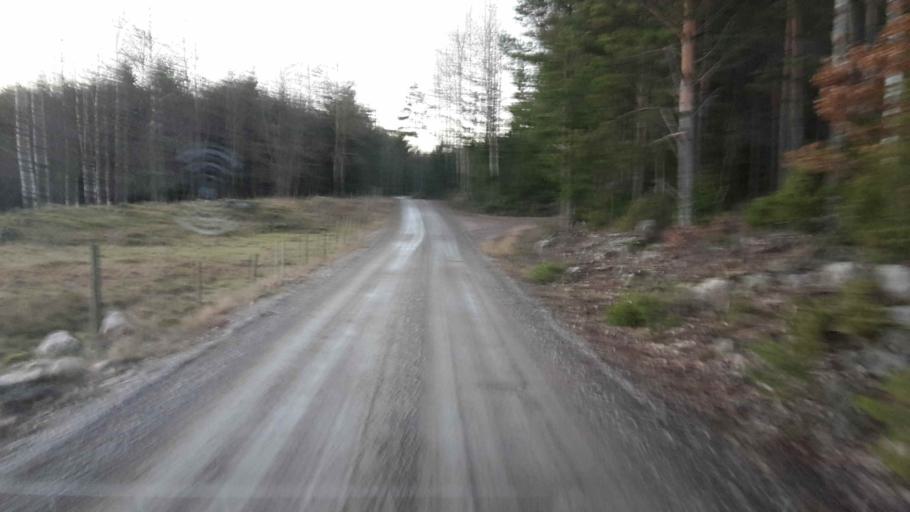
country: SE
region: OEstergoetland
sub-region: Atvidabergs Kommun
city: Atvidaberg
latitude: 58.2624
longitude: 16.0678
